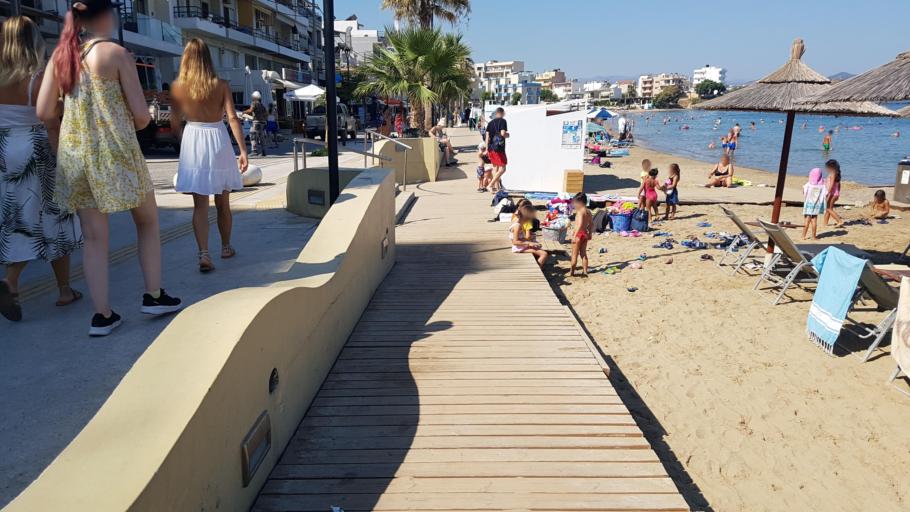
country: GR
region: Crete
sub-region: Nomos Chanias
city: Chania
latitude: 35.5149
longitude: 24.0079
